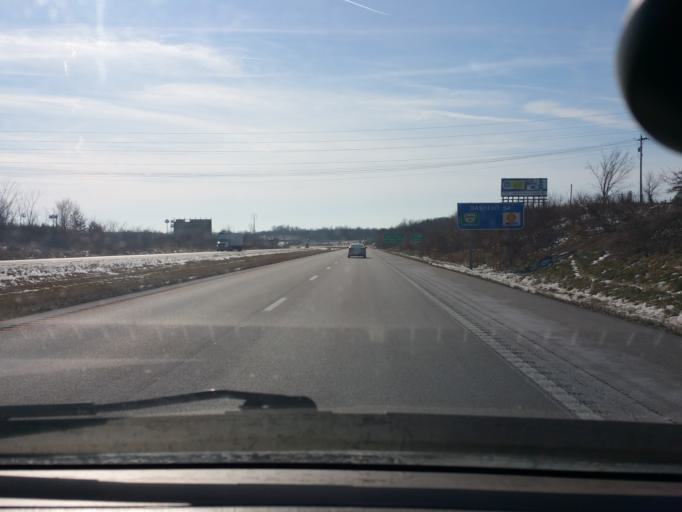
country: US
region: Missouri
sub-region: Clinton County
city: Cameron
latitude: 39.7616
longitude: -94.2177
